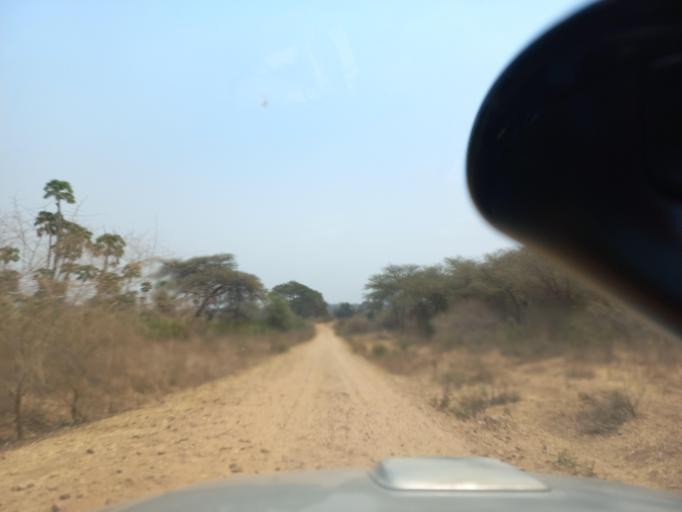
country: ZW
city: Chirundu
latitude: -15.9411
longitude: 28.8257
